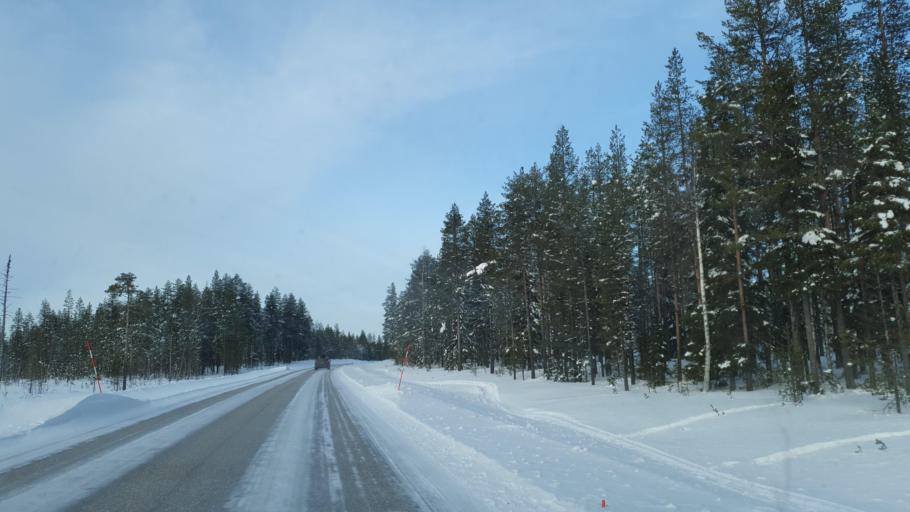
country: FI
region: Lapland
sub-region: Tunturi-Lappi
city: Kolari
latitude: 67.4526
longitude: 23.8449
